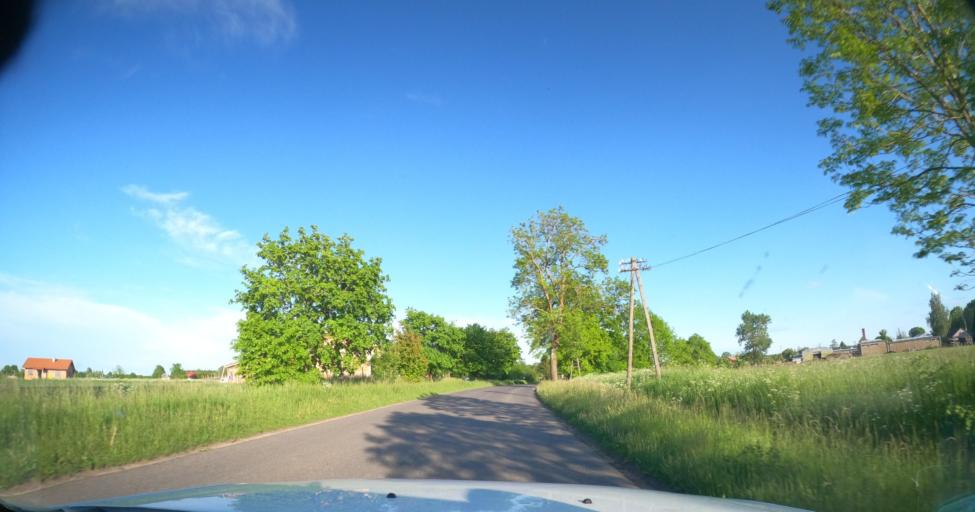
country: PL
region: Warmian-Masurian Voivodeship
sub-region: Powiat braniewski
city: Braniewo
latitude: 54.2733
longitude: 19.9331
